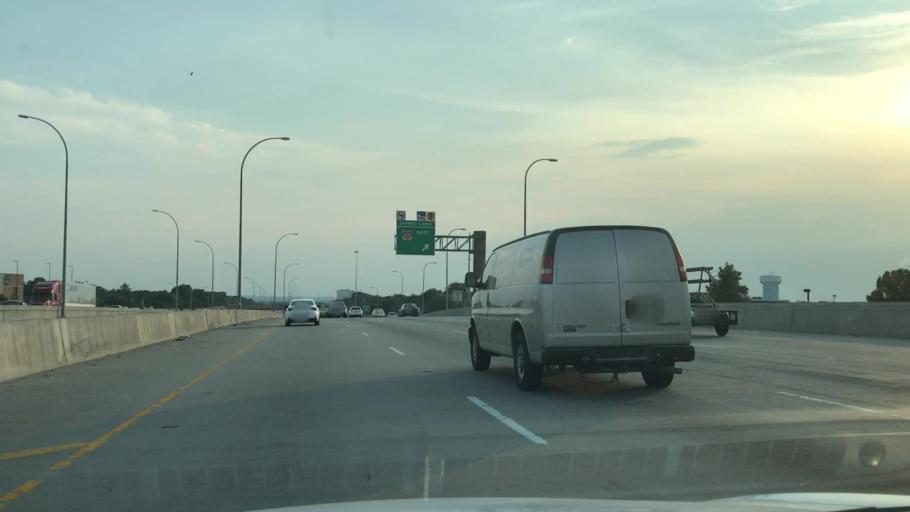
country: US
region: Texas
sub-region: Dallas County
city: Farmers Branch
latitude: 32.9075
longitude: -96.8723
